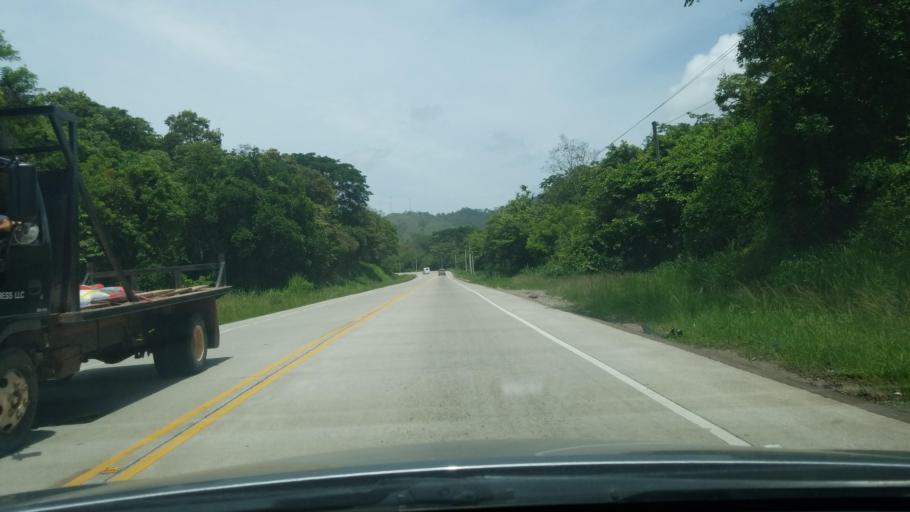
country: HN
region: Copan
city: Agua Caliente
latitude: 14.8731
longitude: -88.7788
